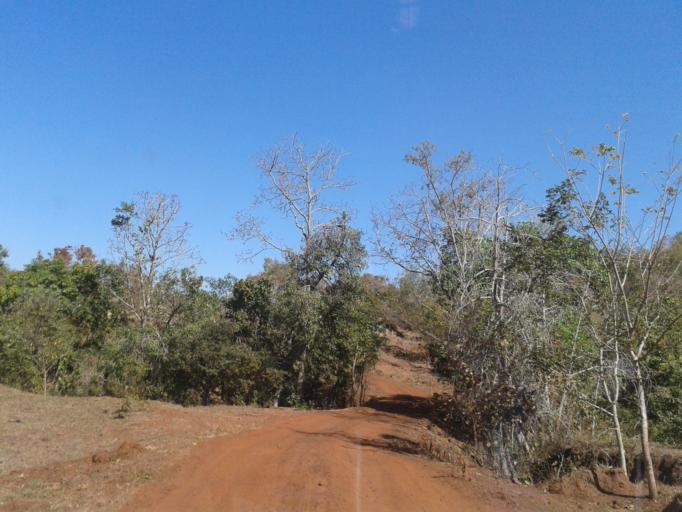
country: BR
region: Minas Gerais
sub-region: Santa Vitoria
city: Santa Vitoria
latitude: -19.0986
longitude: -49.9750
